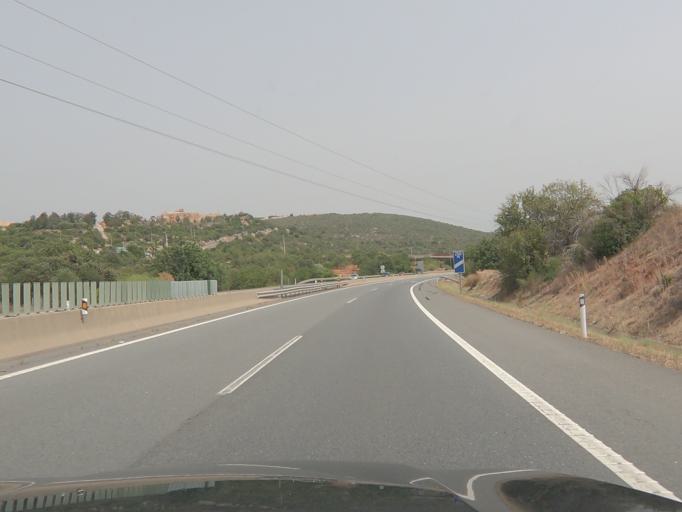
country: PT
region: Faro
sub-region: Loule
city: Boliqueime
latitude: 37.1502
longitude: -8.1302
